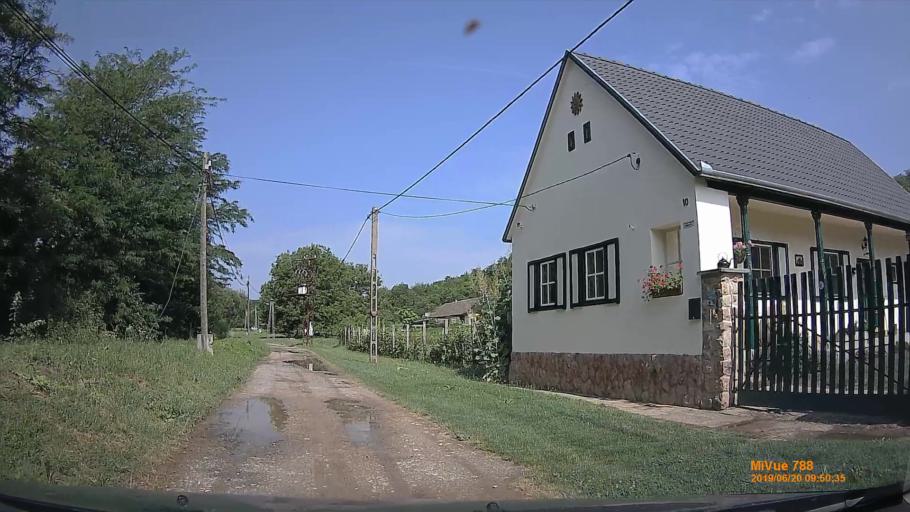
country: HU
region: Baranya
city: Pecsvarad
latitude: 46.1731
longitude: 18.4716
